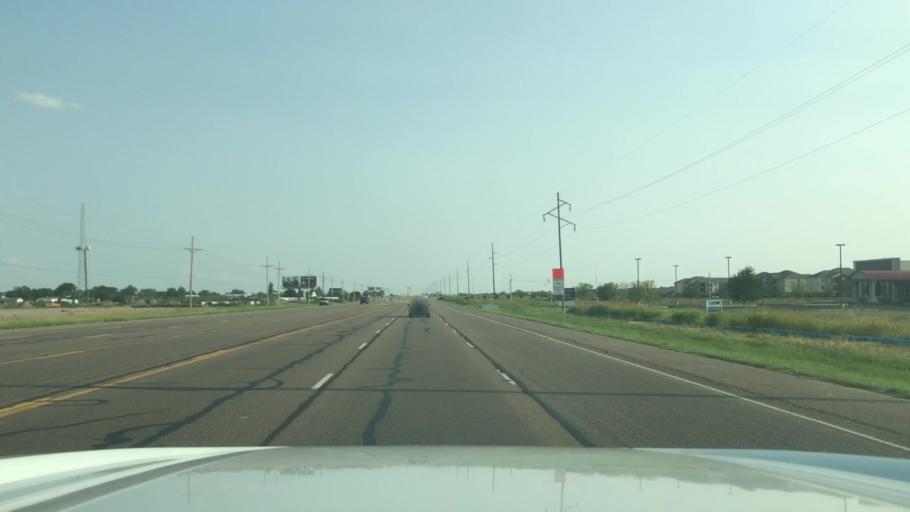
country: US
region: Texas
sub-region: Potter County
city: Amarillo
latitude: 35.1352
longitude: -101.9382
